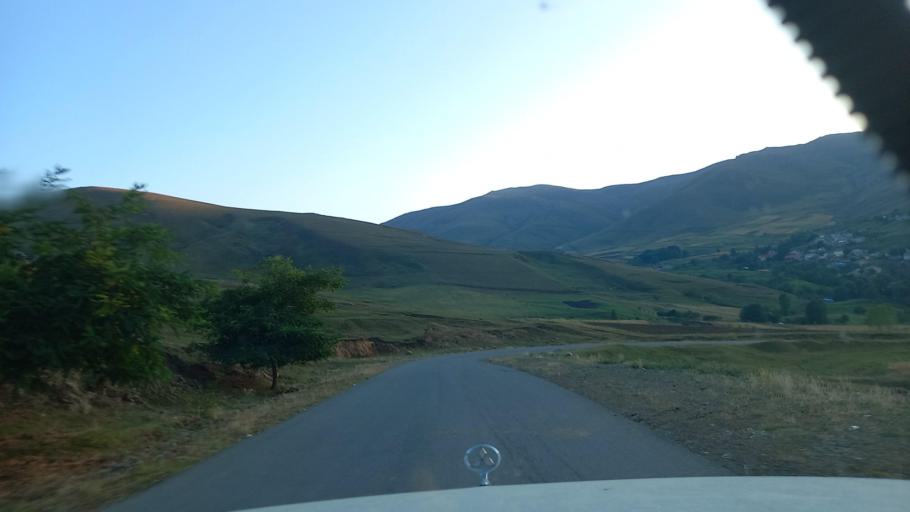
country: AZ
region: Tovuz
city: Cobansignaq
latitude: 40.6837
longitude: 45.7712
